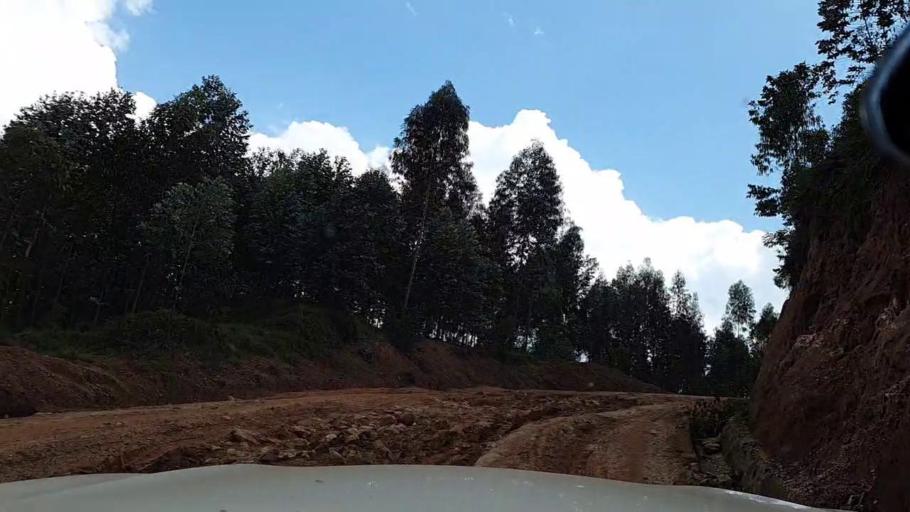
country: RW
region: Southern Province
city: Nzega
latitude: -2.7001
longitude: 29.4380
